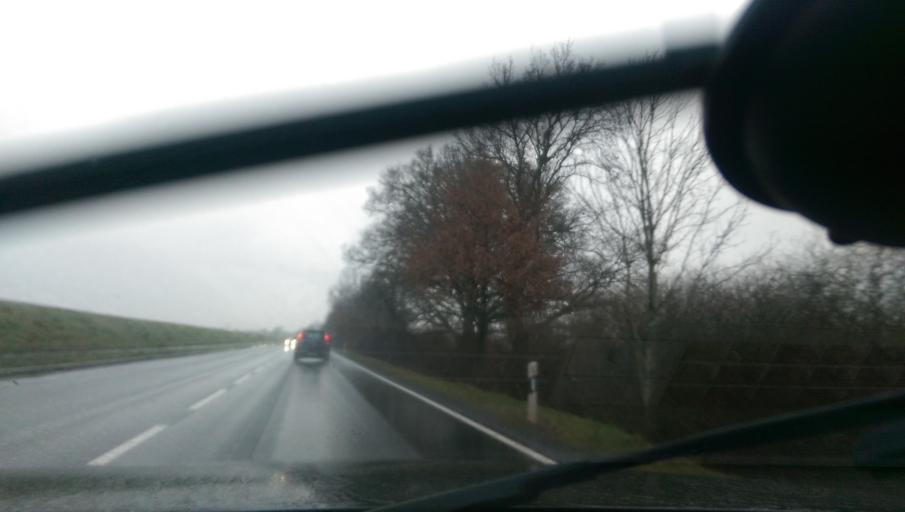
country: DE
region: Lower Saxony
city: Dorverden
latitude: 52.8753
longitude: 9.2263
